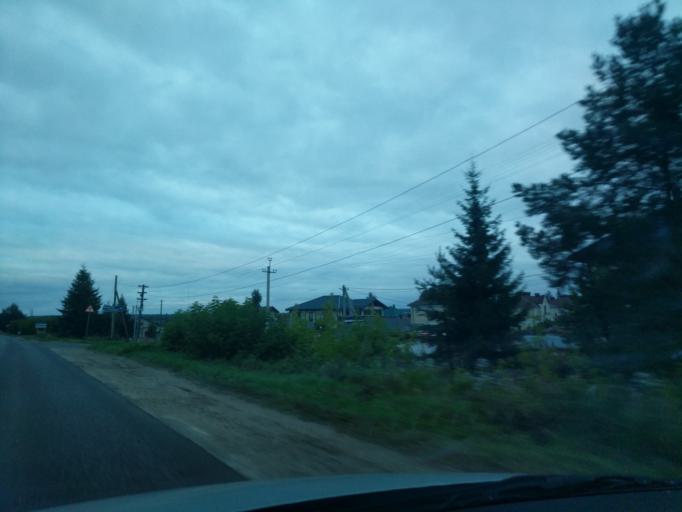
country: RU
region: Kirov
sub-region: Kirovo-Chepetskiy Rayon
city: Kirov
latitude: 58.6029
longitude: 49.8204
